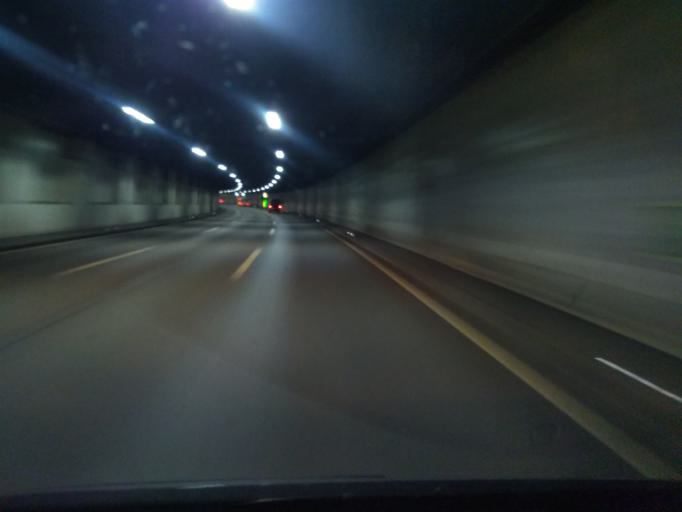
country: CH
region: Basel-Landschaft
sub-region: Bezirk Arlesheim
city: Muttenz
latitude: 47.5322
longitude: 7.6612
